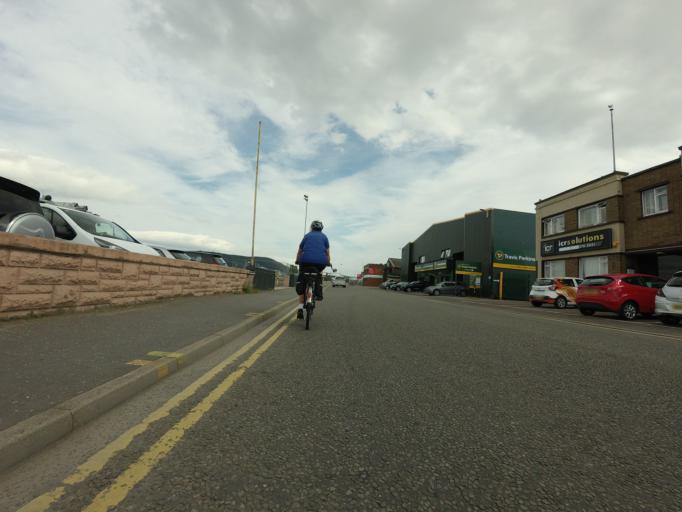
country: GB
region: Scotland
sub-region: Highland
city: Inverness
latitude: 57.4843
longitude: -4.2298
